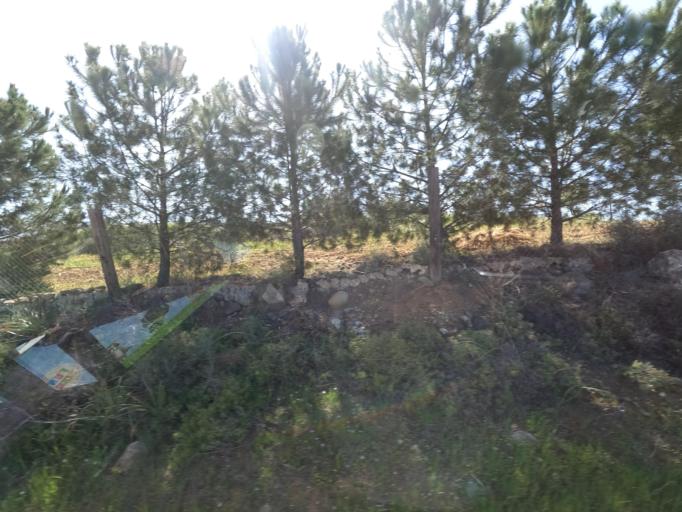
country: CY
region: Lefkosia
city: Astromeritis
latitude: 35.0862
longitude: 33.0196
